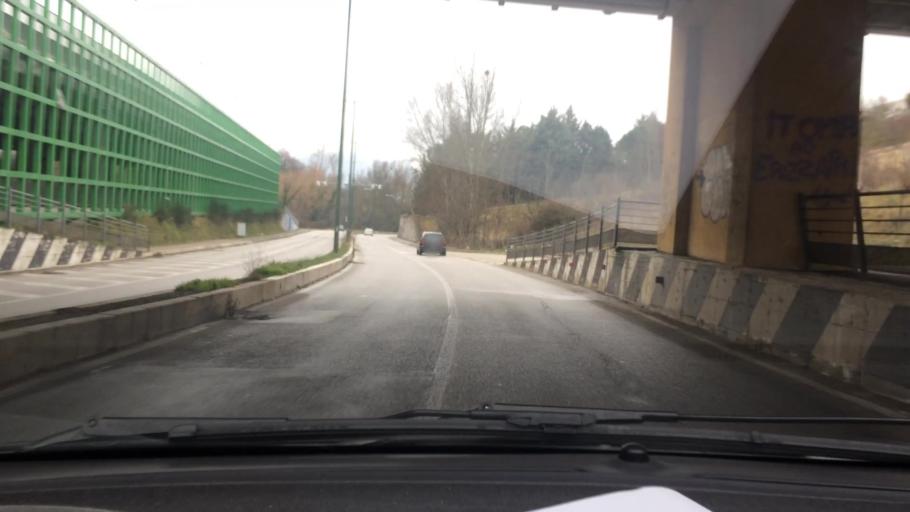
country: IT
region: Basilicate
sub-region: Provincia di Potenza
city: Potenza
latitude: 40.6370
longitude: 15.7954
